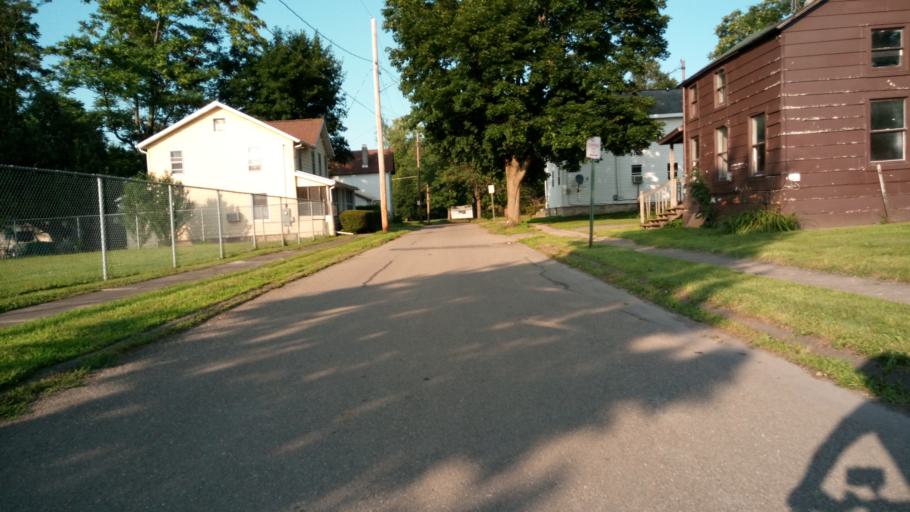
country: US
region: New York
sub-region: Chemung County
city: Elmira
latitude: 42.0962
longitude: -76.7984
